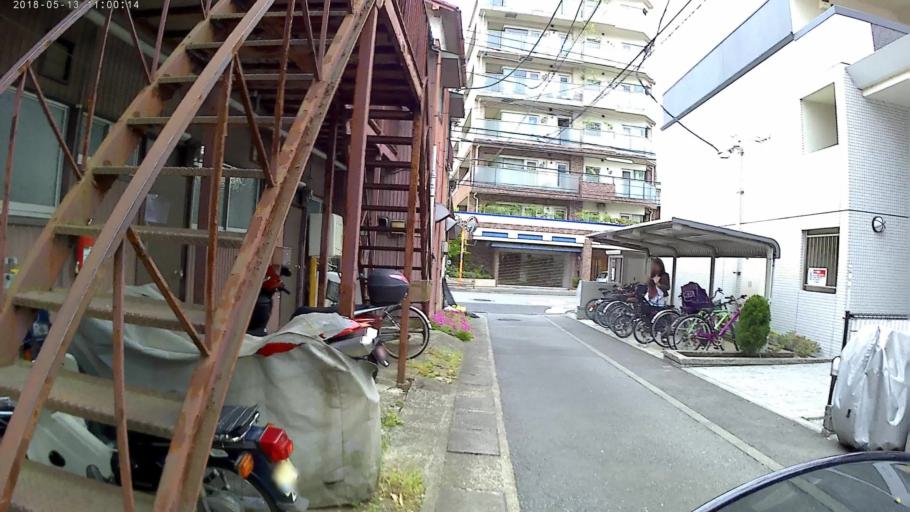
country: JP
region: Tokyo
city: Chofugaoka
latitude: 35.5995
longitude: 139.5974
